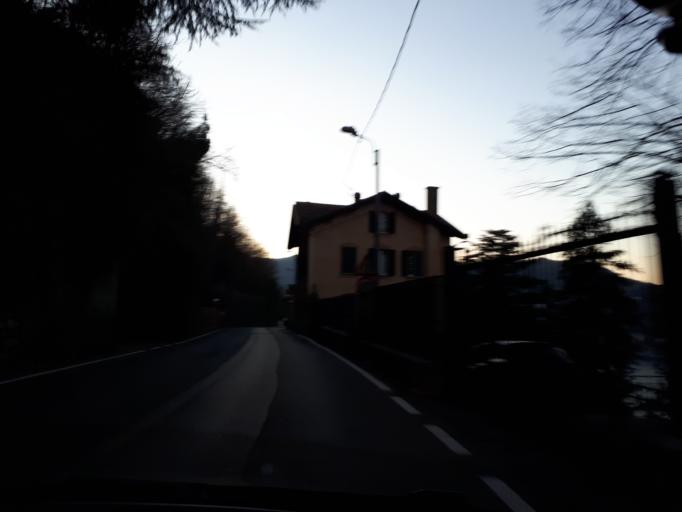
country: IT
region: Lombardy
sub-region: Provincia di Como
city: Brunate
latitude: 45.8262
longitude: 9.0842
